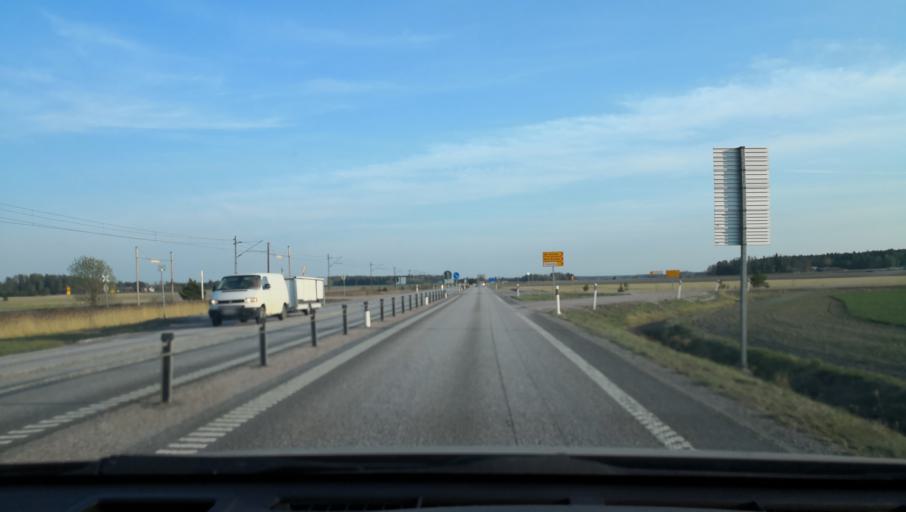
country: SE
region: Vaestmanland
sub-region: Sala Kommun
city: Sala
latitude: 59.8950
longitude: 16.6224
